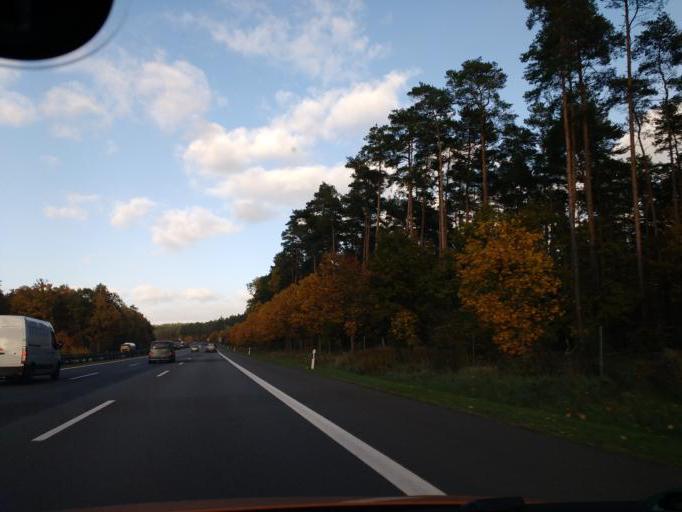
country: DE
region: Brandenburg
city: Grunheide
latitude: 52.4375
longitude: 13.7974
